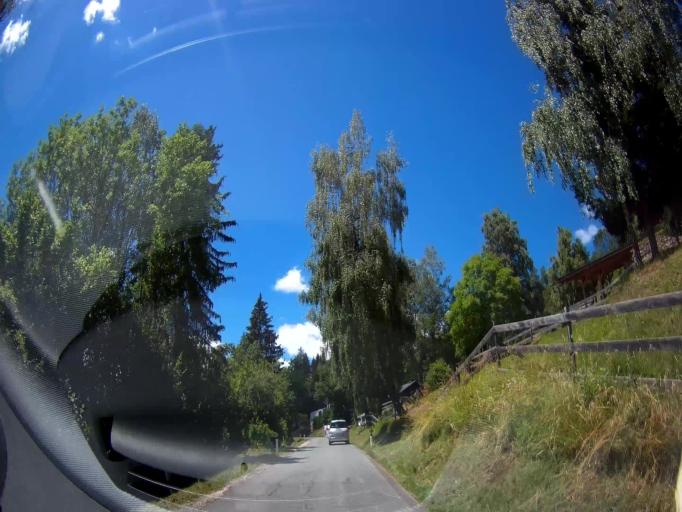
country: AT
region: Carinthia
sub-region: Politischer Bezirk Sankt Veit an der Glan
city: St. Georgen am Laengsee
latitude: 46.7244
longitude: 14.4308
